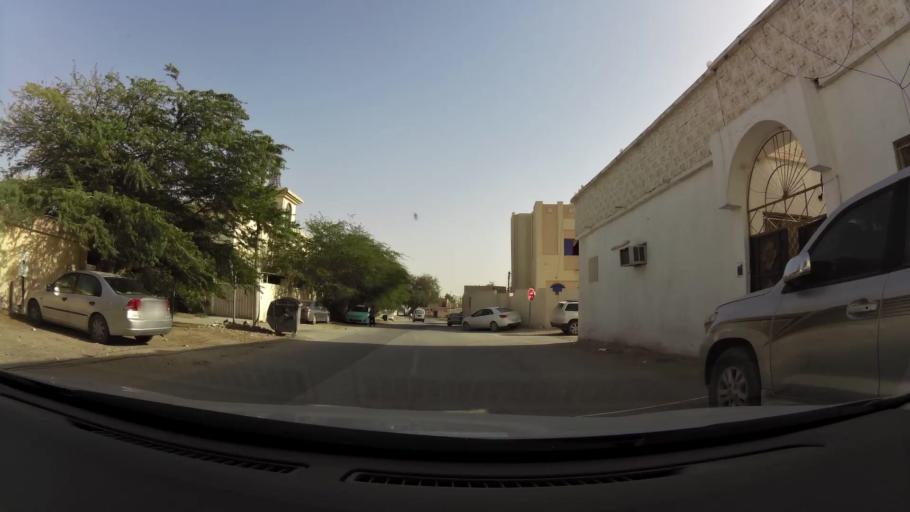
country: QA
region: Baladiyat ar Rayyan
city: Ar Rayyan
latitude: 25.3366
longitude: 51.4446
